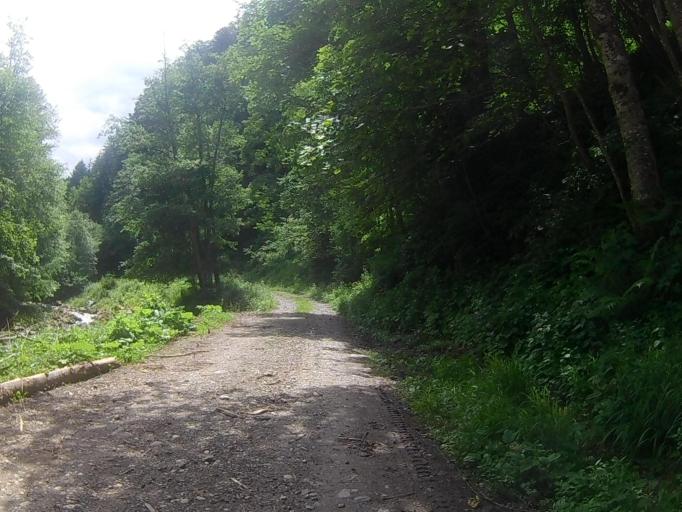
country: SI
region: Selnica ob Dravi
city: Selnica ob Dravi
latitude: 46.5119
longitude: 15.4578
